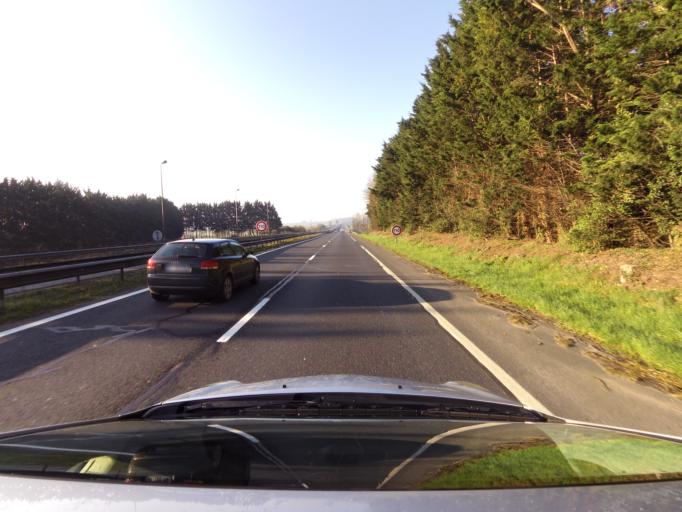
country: FR
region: Lower Normandy
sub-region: Departement du Calvados
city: Saint-Germain-la-Blanche-Herbe
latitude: 49.1865
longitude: -0.4248
